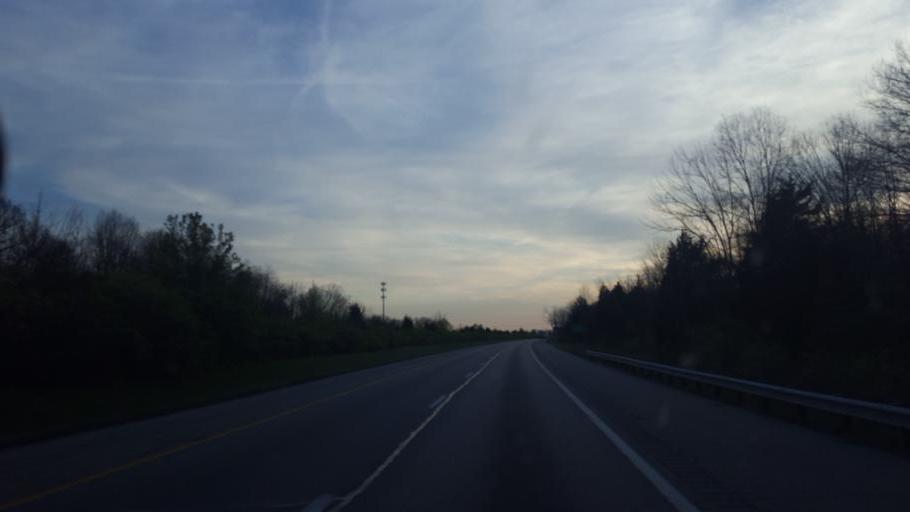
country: US
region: Ohio
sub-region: Warren County
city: South Lebanon
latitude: 39.3870
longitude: -84.2093
